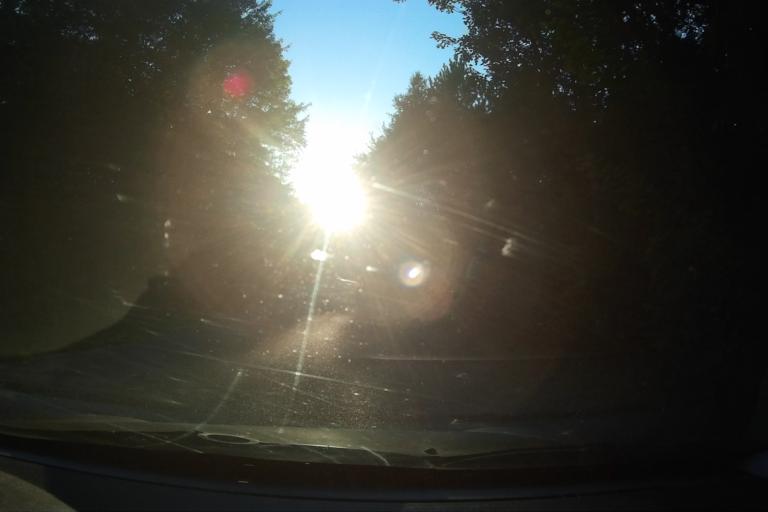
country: CA
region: Ontario
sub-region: Algoma
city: Sault Ste. Marie
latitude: 46.9699
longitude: -84.6897
